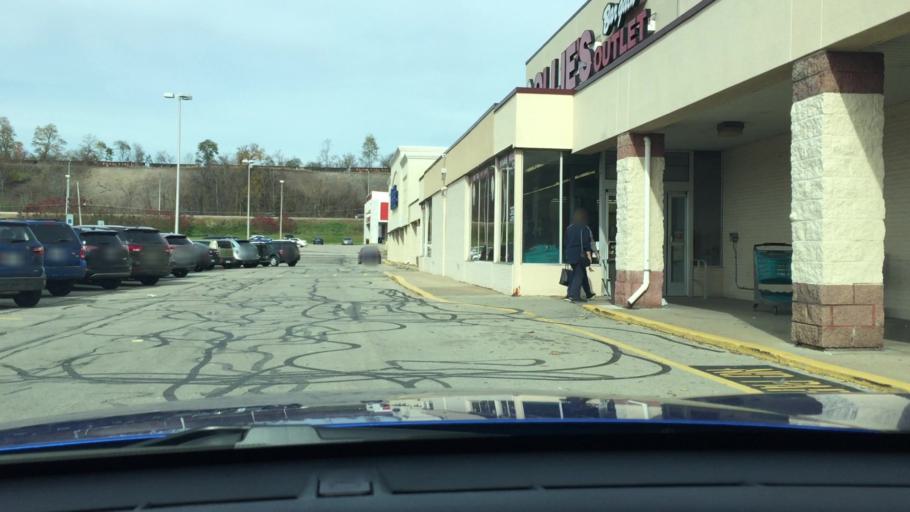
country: US
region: Pennsylvania
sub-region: Westmoreland County
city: Lynnwood-Pricedale
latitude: 40.1383
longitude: -79.8391
